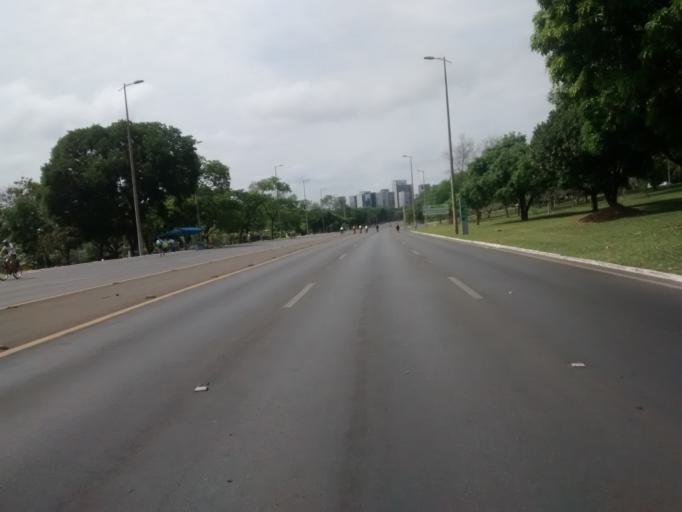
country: BR
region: Federal District
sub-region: Brasilia
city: Brasilia
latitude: -15.7728
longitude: -47.8815
